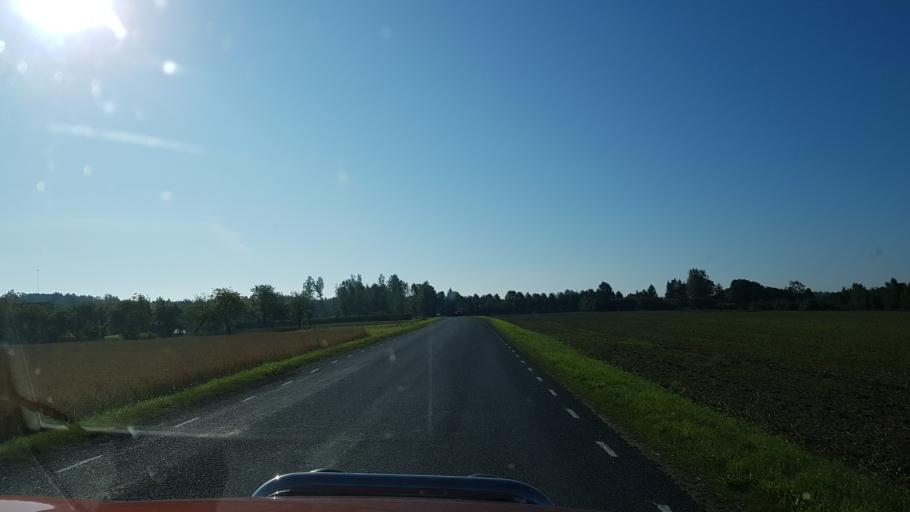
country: EE
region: Jogevamaa
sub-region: Tabivere vald
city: Tabivere
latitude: 58.6918
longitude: 26.5678
